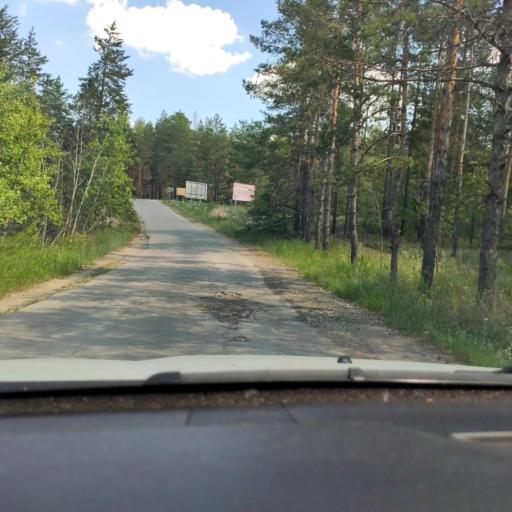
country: RU
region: Samara
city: Pribrezhnyy
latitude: 53.4778
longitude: 49.8220
